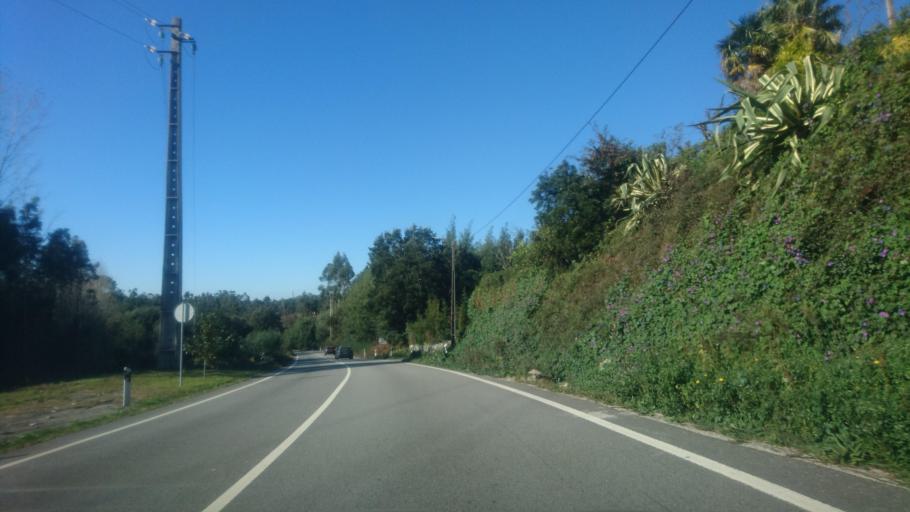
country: PT
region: Aveiro
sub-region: Oliveira de Azemeis
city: Sao Roque
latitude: 40.8891
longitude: -8.4600
